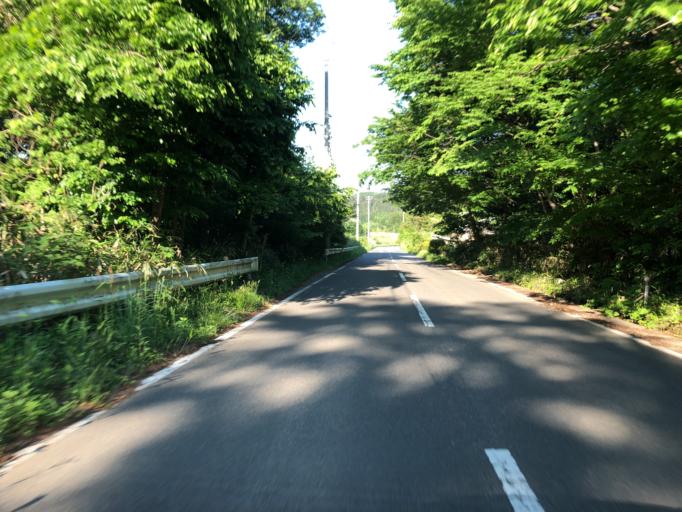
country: JP
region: Fukushima
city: Fukushima-shi
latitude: 37.7051
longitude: 140.3759
